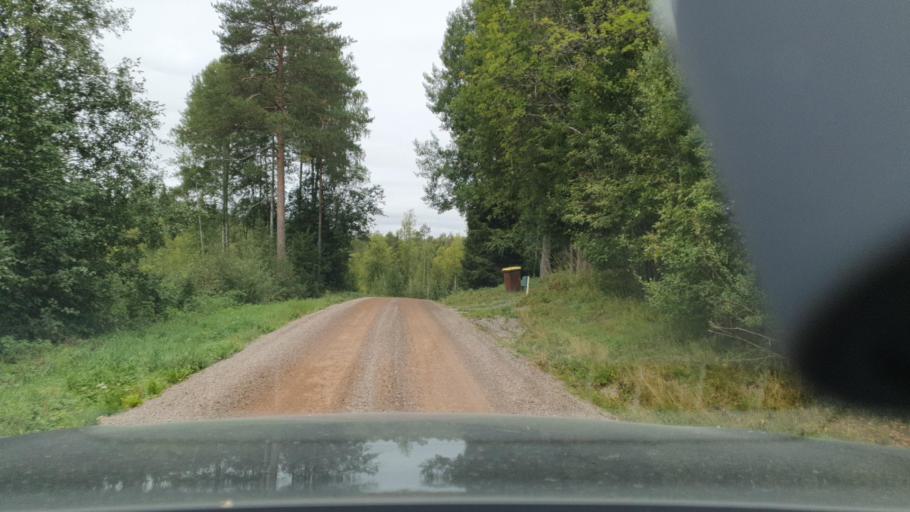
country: SE
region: Vaermland
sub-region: Eda Kommun
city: Charlottenberg
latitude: 60.0896
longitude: 12.5055
